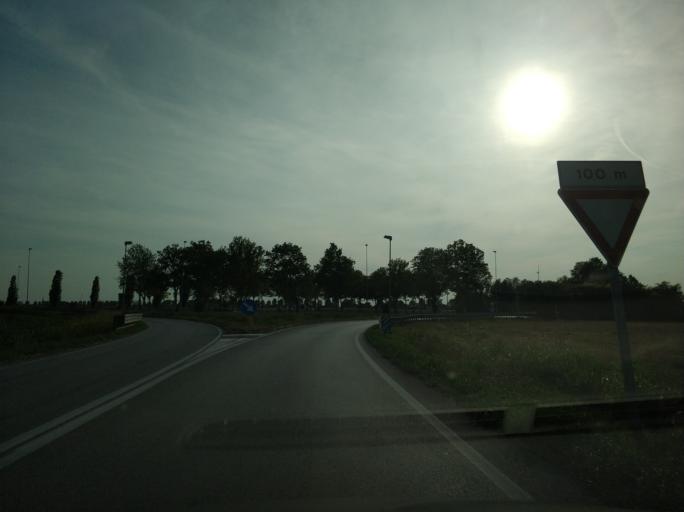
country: IT
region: Veneto
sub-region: Provincia di Venezia
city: Pegolotte
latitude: 45.2143
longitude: 12.0412
